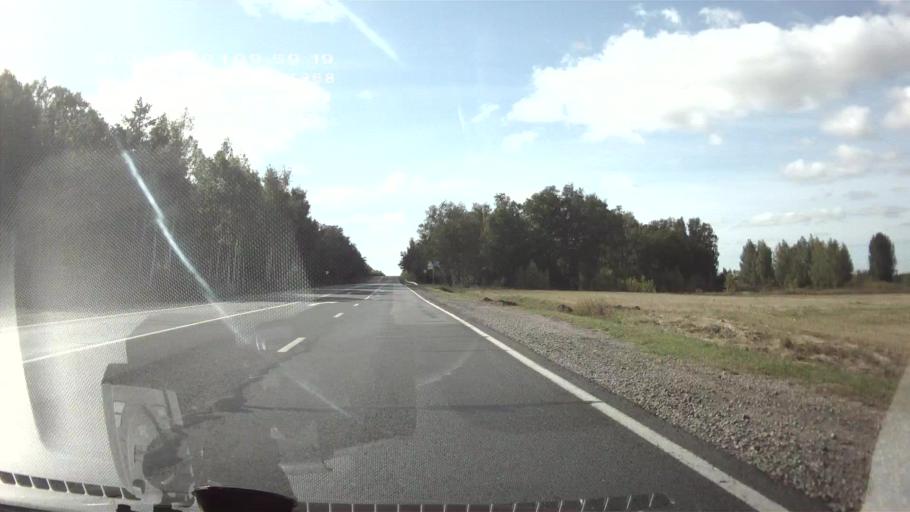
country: RU
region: Ulyanovsk
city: Krasnyy Gulyay
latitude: 54.0800
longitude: 48.2278
